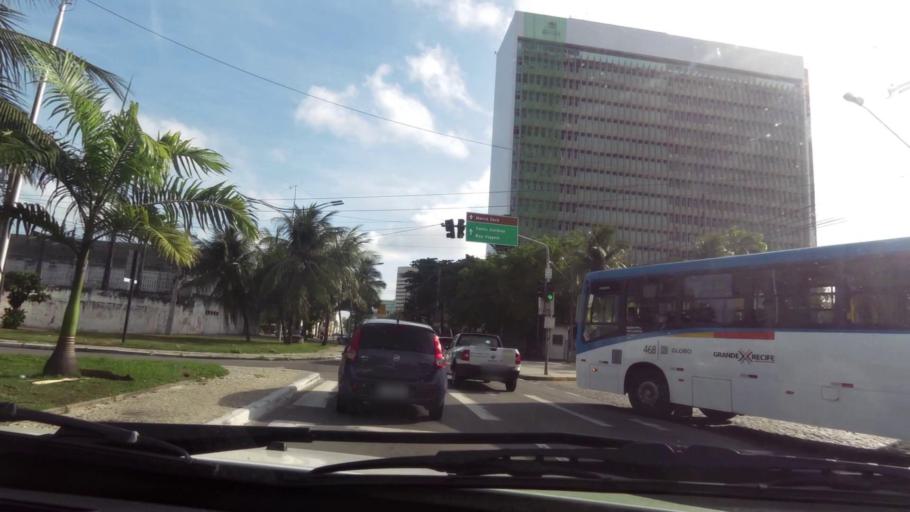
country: BR
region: Pernambuco
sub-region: Recife
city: Recife
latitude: -8.0542
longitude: -34.8720
